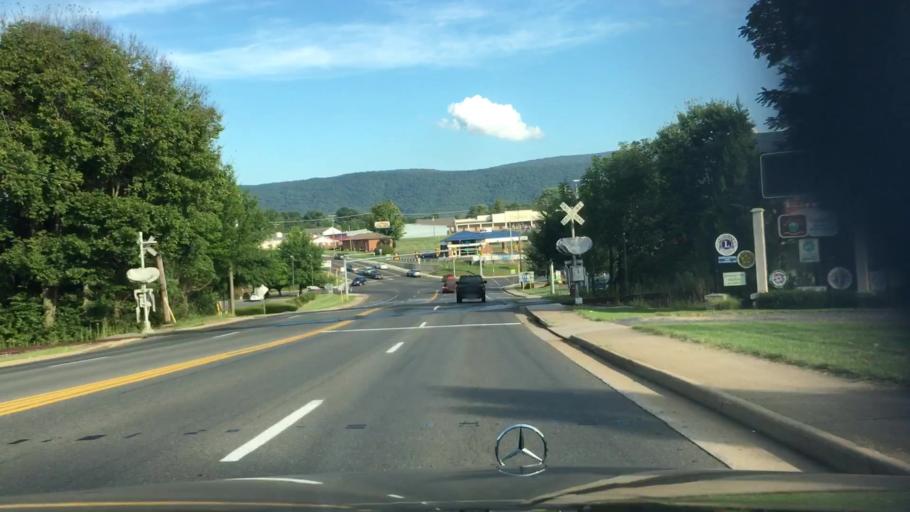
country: US
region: Virginia
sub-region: Shenandoah County
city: Woodstock
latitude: 38.8678
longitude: -78.5197
